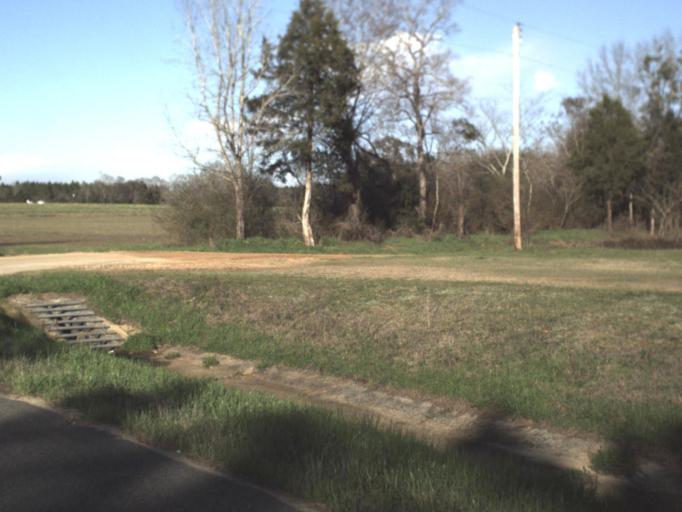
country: US
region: Florida
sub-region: Jackson County
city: Marianna
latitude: 30.6965
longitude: -85.2335
